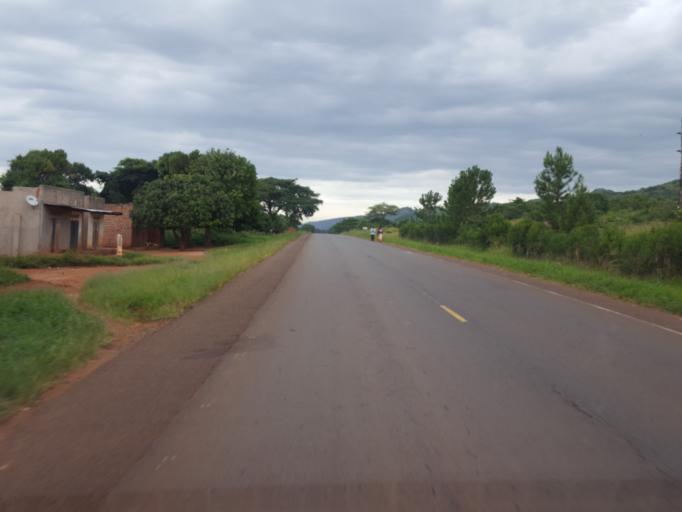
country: UG
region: Central Region
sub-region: Kiboga District
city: Kiboga
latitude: 0.8634
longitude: 31.8599
